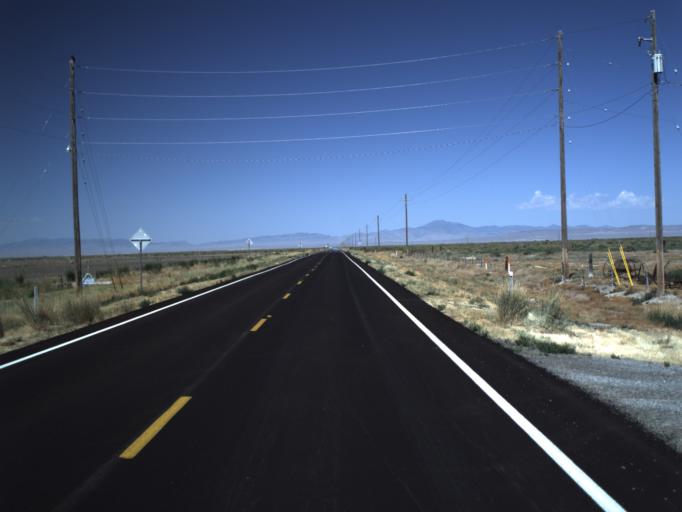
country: US
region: Utah
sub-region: Millard County
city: Delta
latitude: 39.3309
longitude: -112.6833
